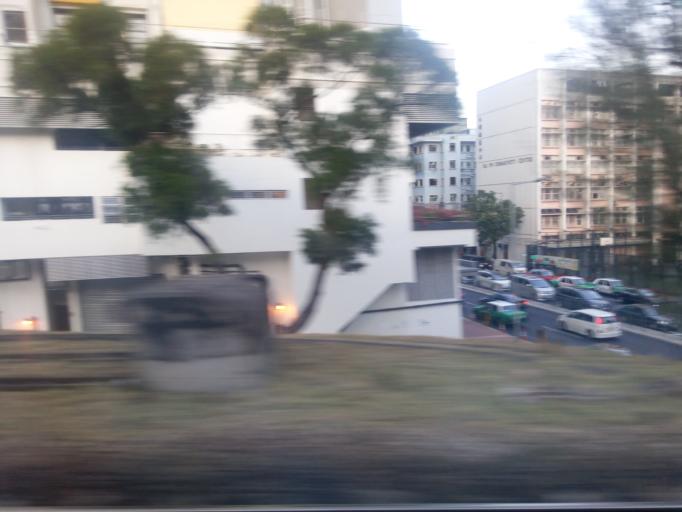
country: HK
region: Tai Po
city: Tai Po
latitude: 22.4465
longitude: 114.1651
